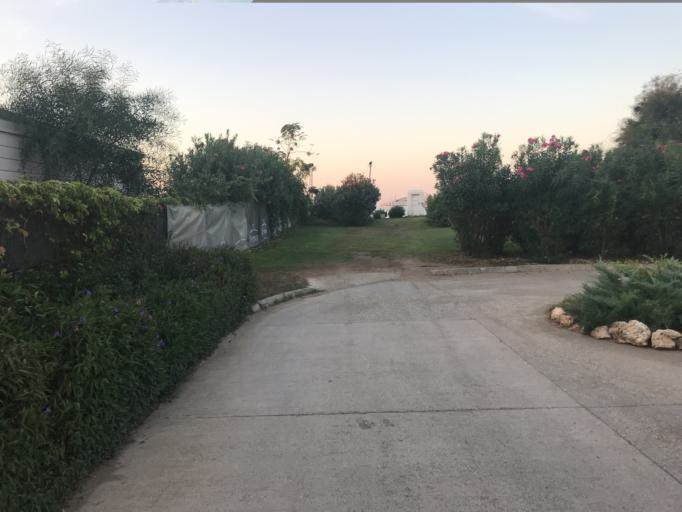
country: TR
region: Antalya
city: Belek
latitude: 36.8578
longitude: 31.0121
